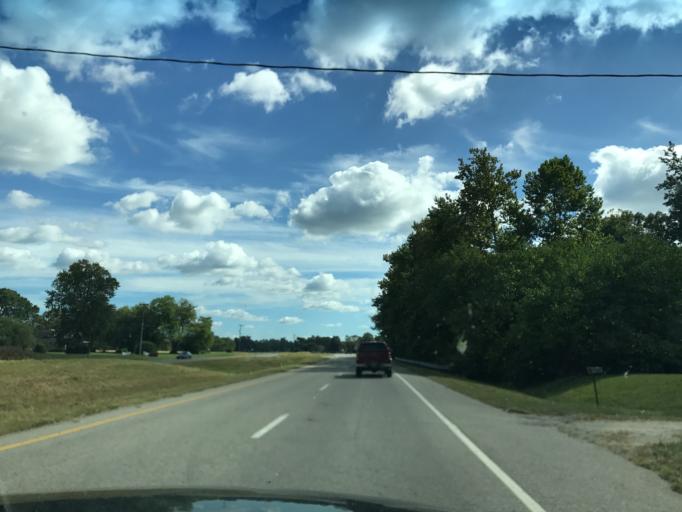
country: US
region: Virginia
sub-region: Middlesex County
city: Saluda
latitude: 37.6830
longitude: -76.6814
